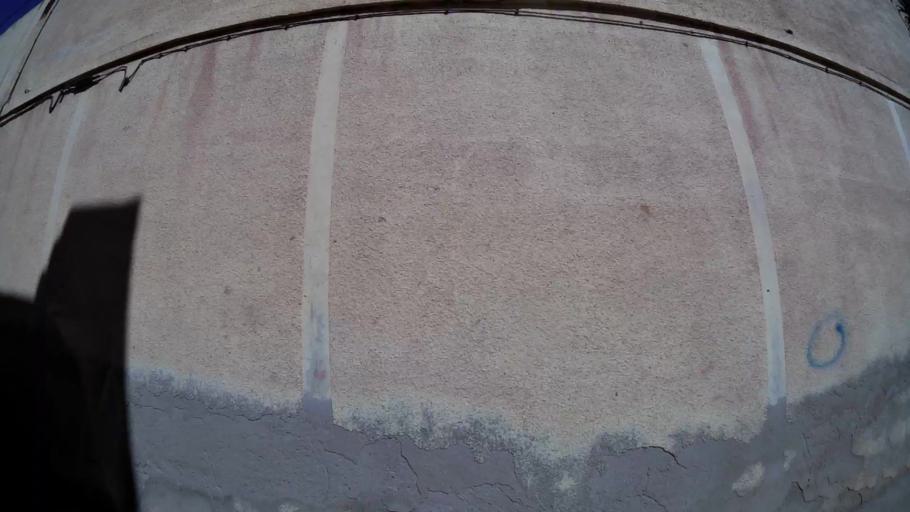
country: MA
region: Oriental
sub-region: Oujda-Angad
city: Oujda
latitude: 34.6894
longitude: -1.9272
